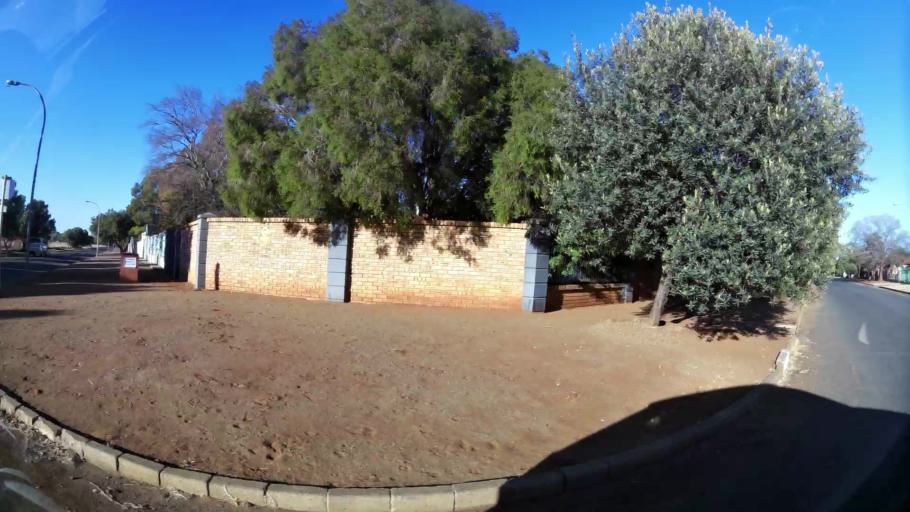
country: ZA
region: Northern Cape
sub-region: Frances Baard District Municipality
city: Kimberley
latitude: -28.7485
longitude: 24.7245
